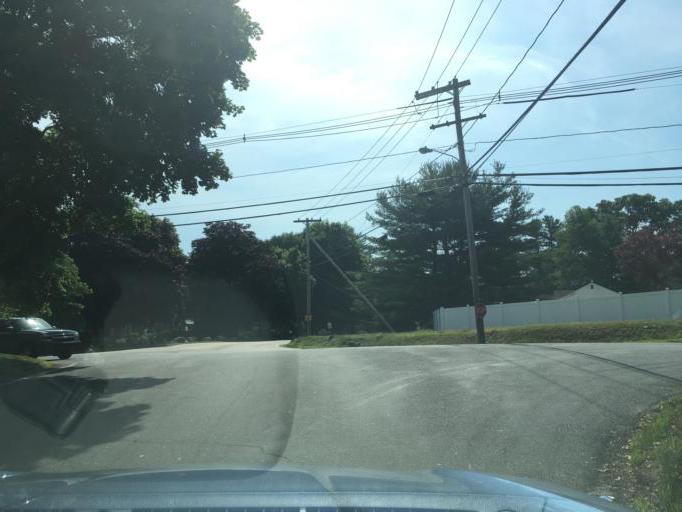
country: US
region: Rhode Island
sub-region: Washington County
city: Exeter
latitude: 41.5939
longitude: -71.4903
